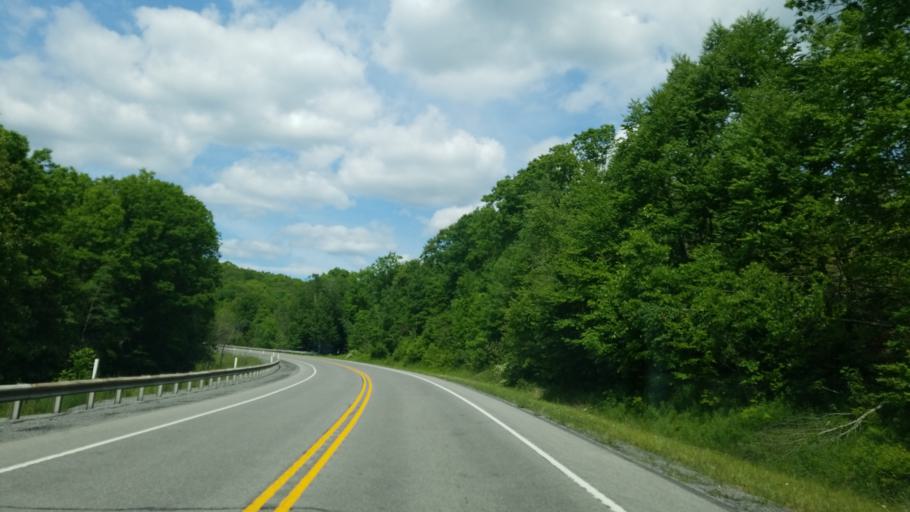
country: US
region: Pennsylvania
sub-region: Clearfield County
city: Clearfield
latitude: 40.9580
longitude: -78.3702
